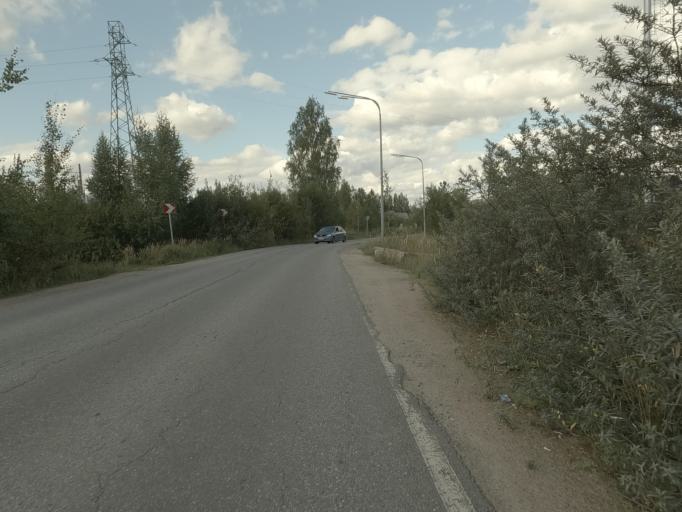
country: RU
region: Leningrad
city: Ul'yanovka
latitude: 59.6311
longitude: 30.7893
